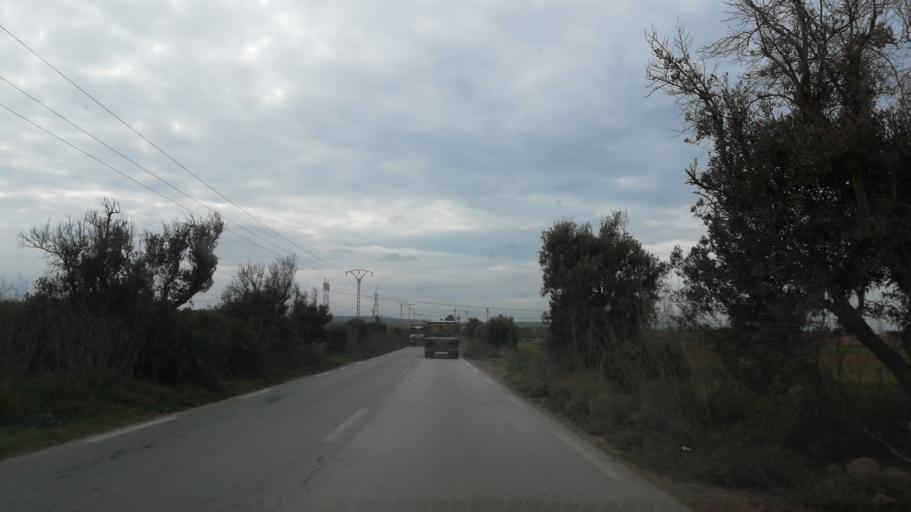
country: DZ
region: Oran
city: Ain el Bya
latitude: 35.7777
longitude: -0.3455
